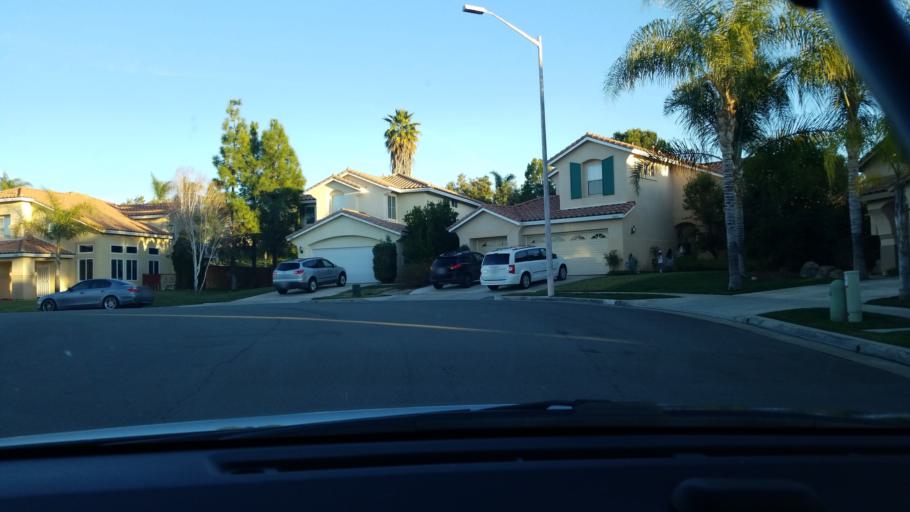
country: US
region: California
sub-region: Riverside County
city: Temecula
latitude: 33.4773
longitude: -117.0831
